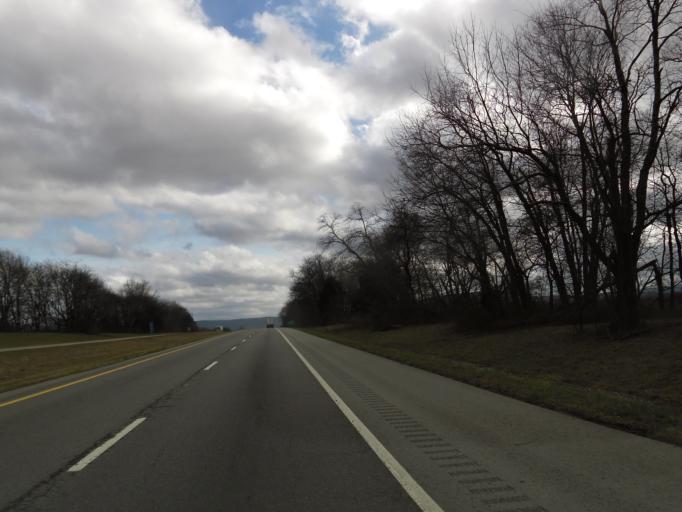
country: US
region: Tennessee
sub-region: Marion County
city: Monteagle
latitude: 35.3115
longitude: -85.9139
